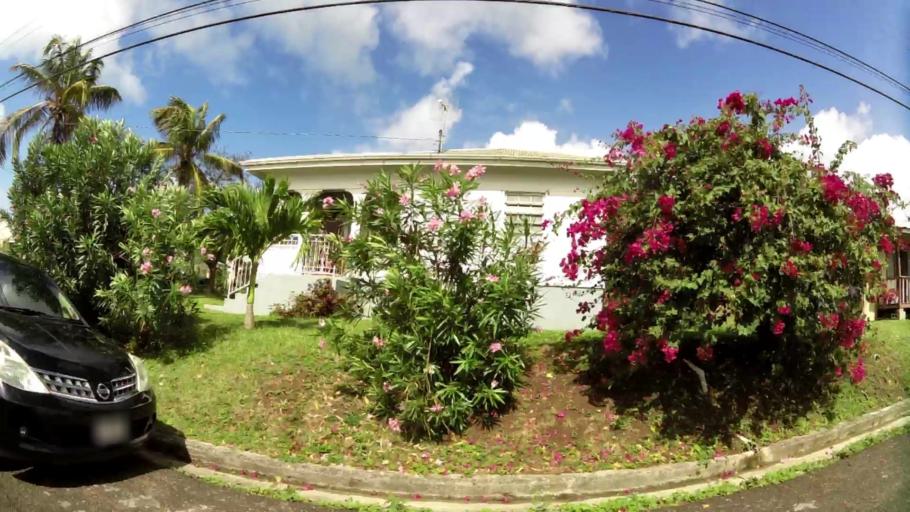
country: AG
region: Saint Mary
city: Bolands
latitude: 17.0782
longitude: -61.8672
